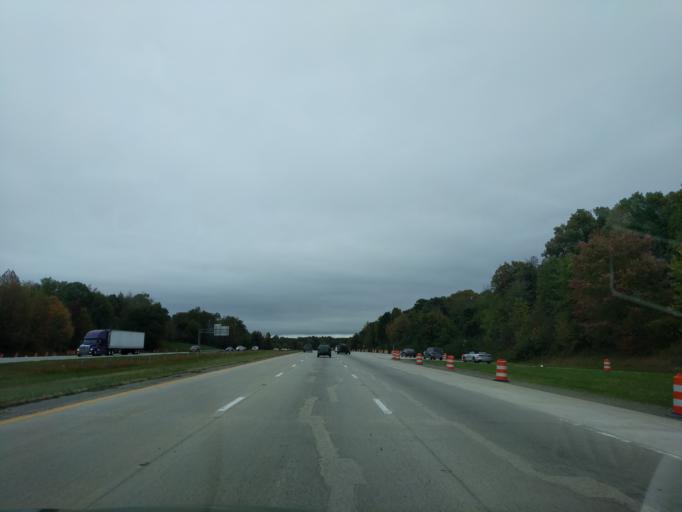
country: US
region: North Carolina
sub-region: Randolph County
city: Archdale
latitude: 35.9049
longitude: -79.9532
